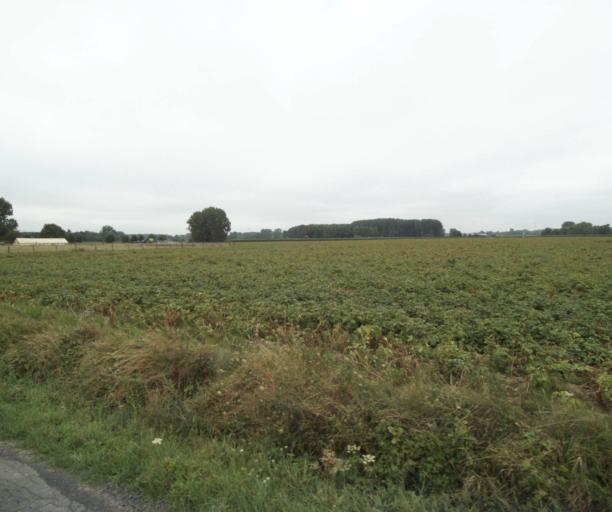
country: FR
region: Nord-Pas-de-Calais
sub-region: Departement du Nord
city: Sailly-lez-Lannoy
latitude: 50.6368
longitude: 3.2131
